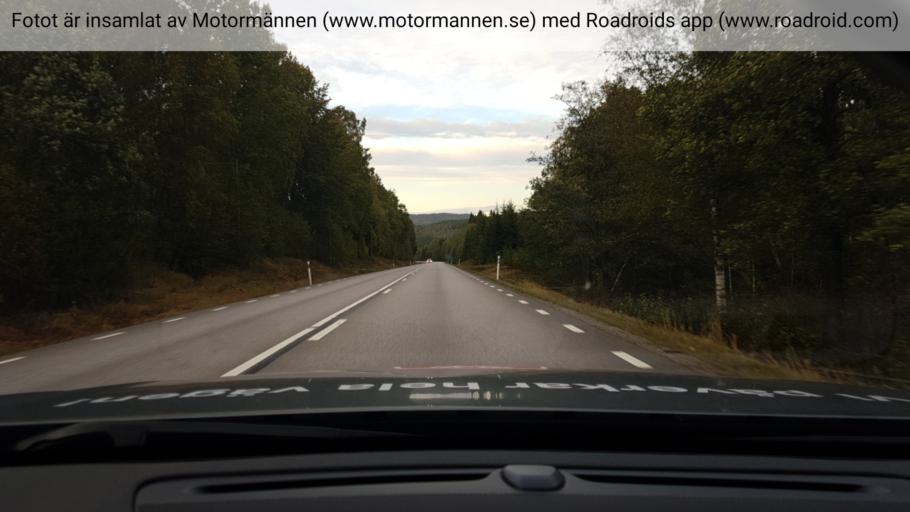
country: SE
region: Vaestra Goetaland
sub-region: Bengtsfors Kommun
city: Dals Langed
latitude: 59.0370
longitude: 12.4241
